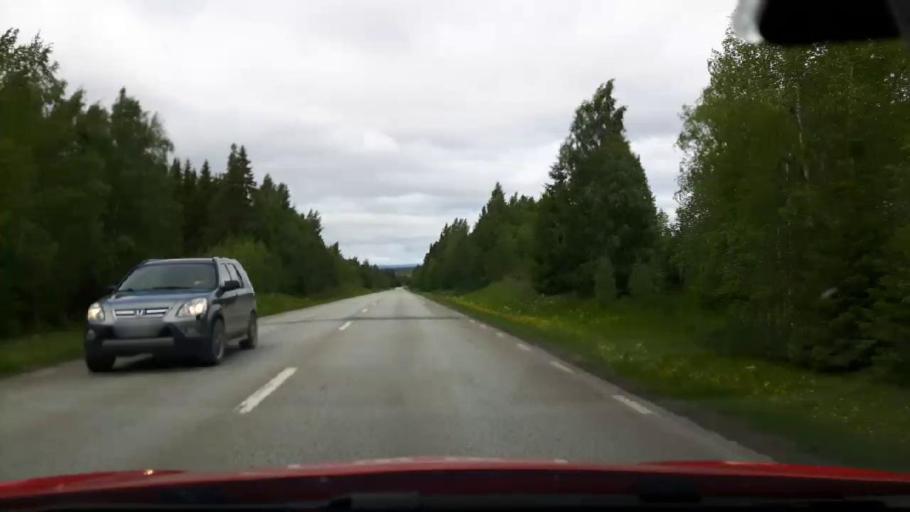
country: SE
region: Jaemtland
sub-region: Krokoms Kommun
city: Krokom
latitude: 63.3930
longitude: 14.5023
